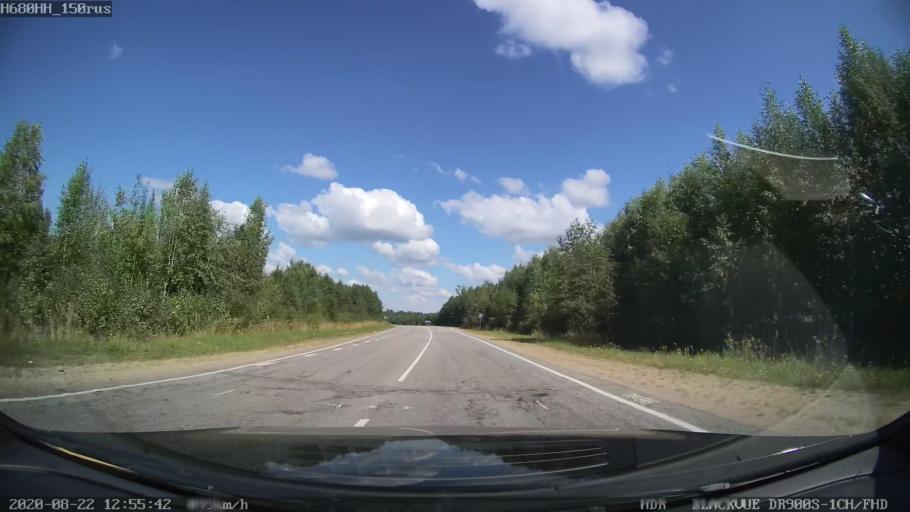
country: RU
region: Tverskaya
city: Rameshki
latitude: 57.5460
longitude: 36.3071
